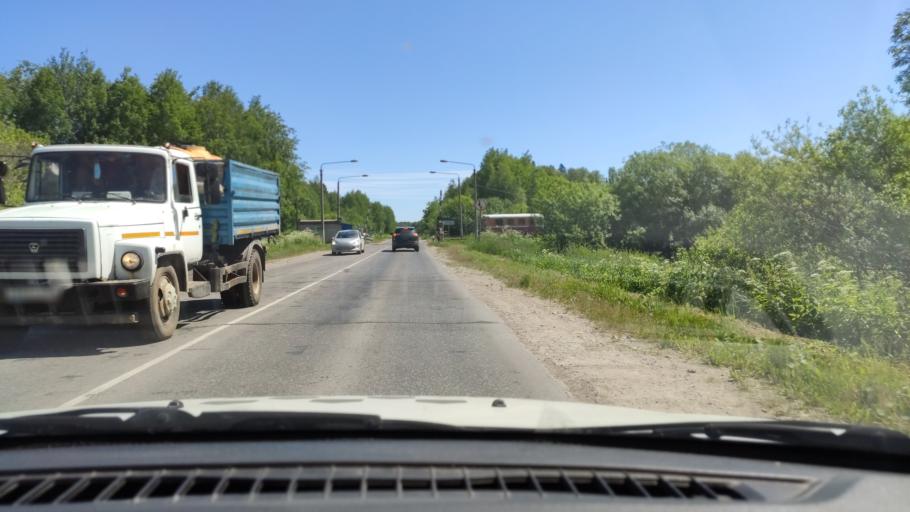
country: RU
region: Perm
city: Novyye Lyady
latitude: 58.0275
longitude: 56.6277
